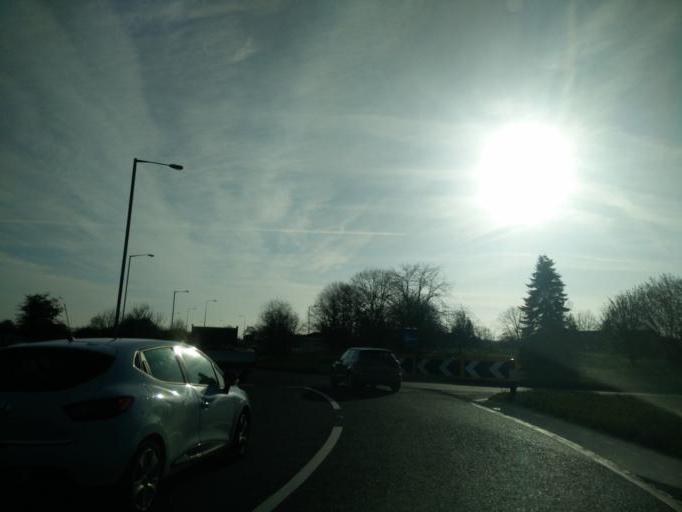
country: GB
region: England
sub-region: County Durham
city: Sedgefield
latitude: 54.6476
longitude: -1.4426
